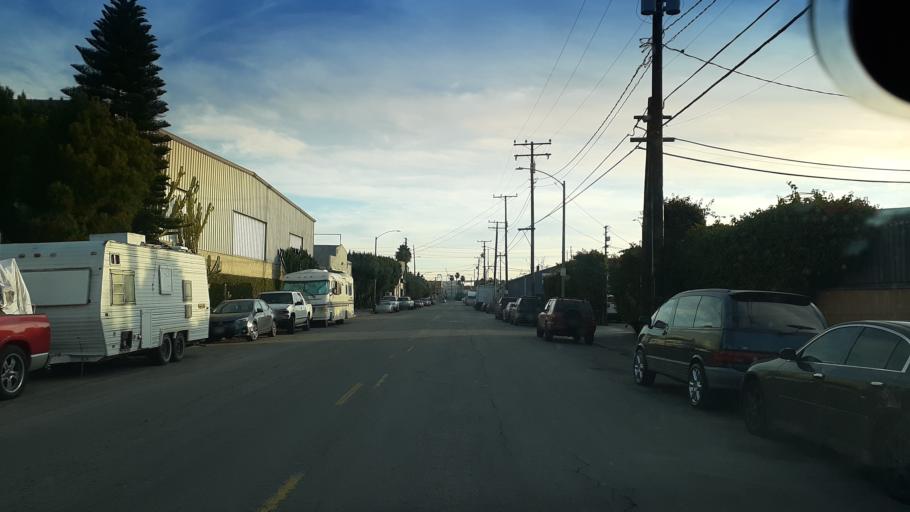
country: US
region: California
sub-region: Los Angeles County
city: Long Beach
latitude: 33.7871
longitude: -118.2188
